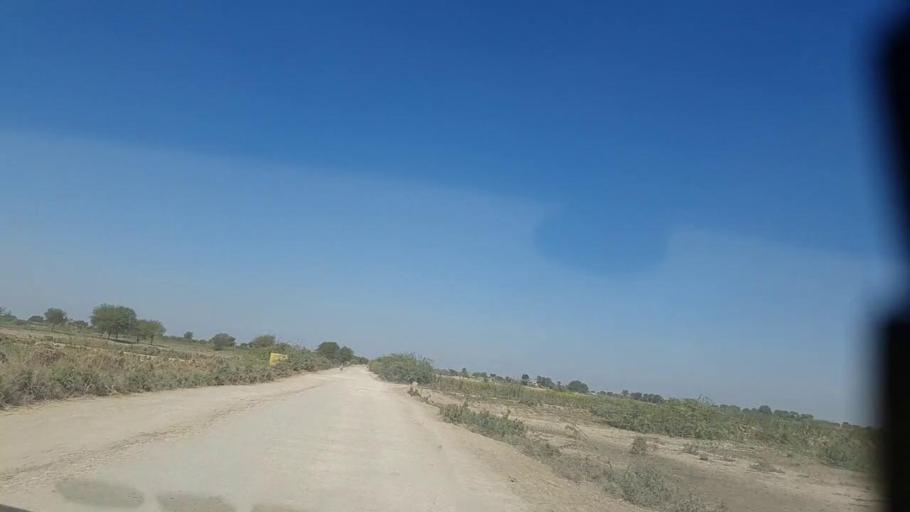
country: PK
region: Sindh
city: Digri
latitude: 25.1747
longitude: 69.0486
